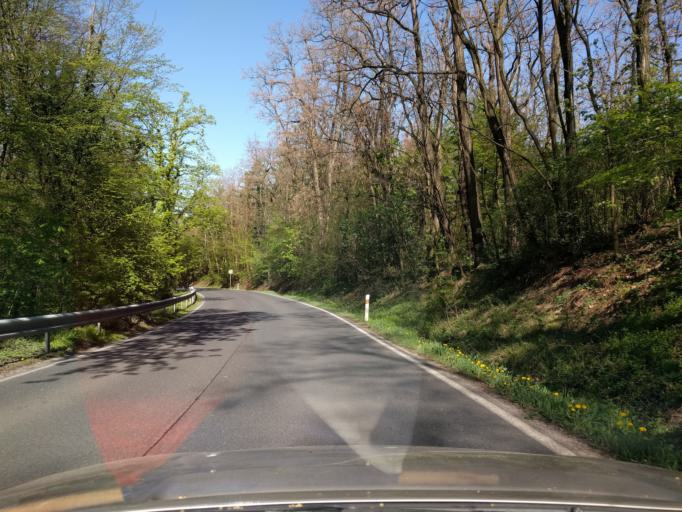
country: CZ
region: Central Bohemia
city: Cesky Brod
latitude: 50.1031
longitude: 14.8580
